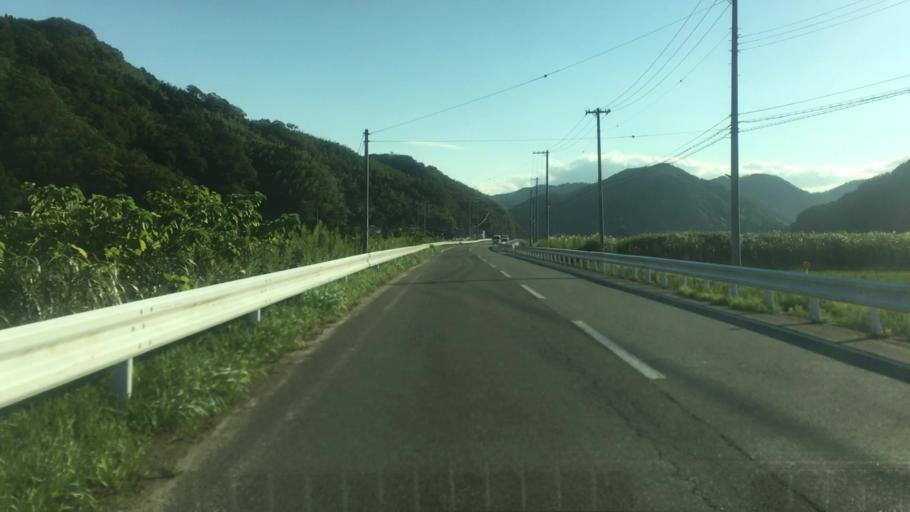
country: JP
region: Hyogo
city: Toyooka
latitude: 35.6172
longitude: 134.8141
